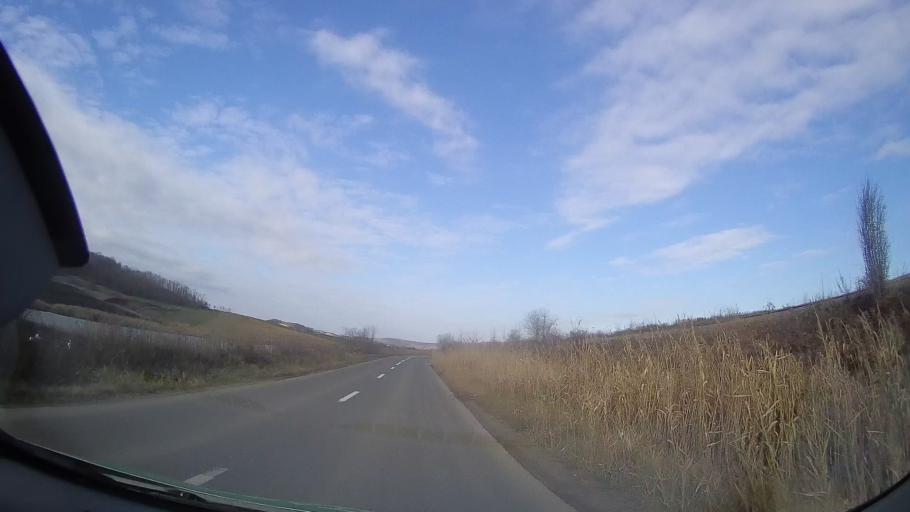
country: RO
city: Barza
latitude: 46.5570
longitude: 24.0995
